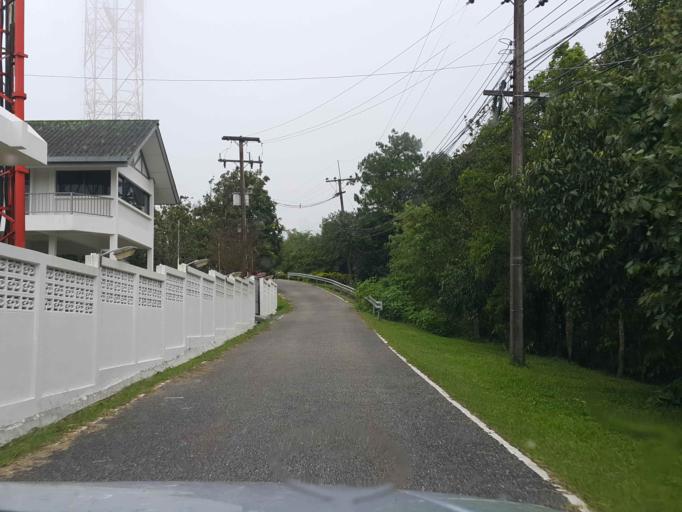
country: TH
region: Tak
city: Tak
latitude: 16.7791
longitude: 98.9272
